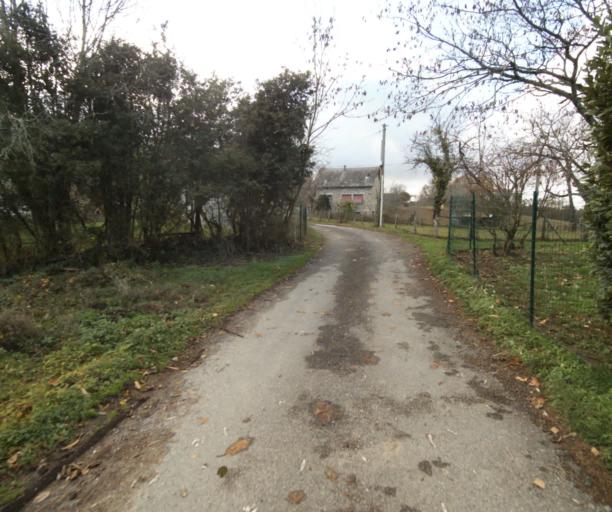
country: FR
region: Limousin
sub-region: Departement de la Correze
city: Laguenne
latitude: 45.2218
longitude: 1.7926
